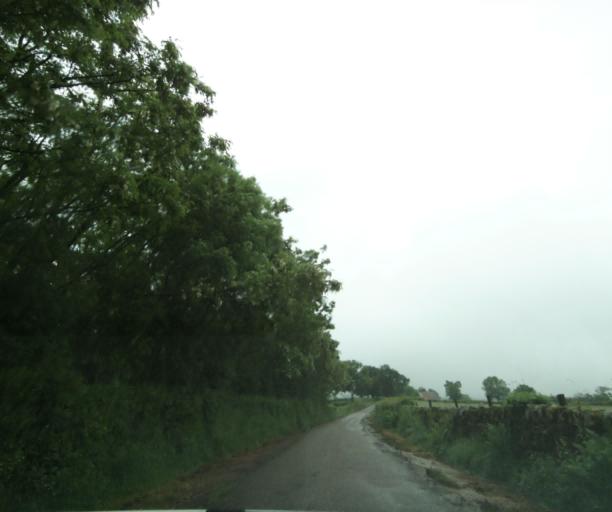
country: FR
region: Bourgogne
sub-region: Departement de Saone-et-Loire
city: La Clayette
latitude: 46.3529
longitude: 4.2468
